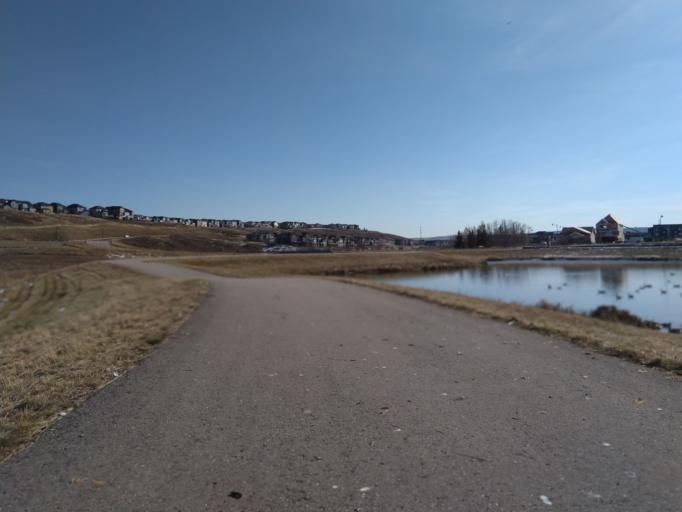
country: CA
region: Alberta
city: Calgary
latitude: 51.1793
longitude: -114.1302
